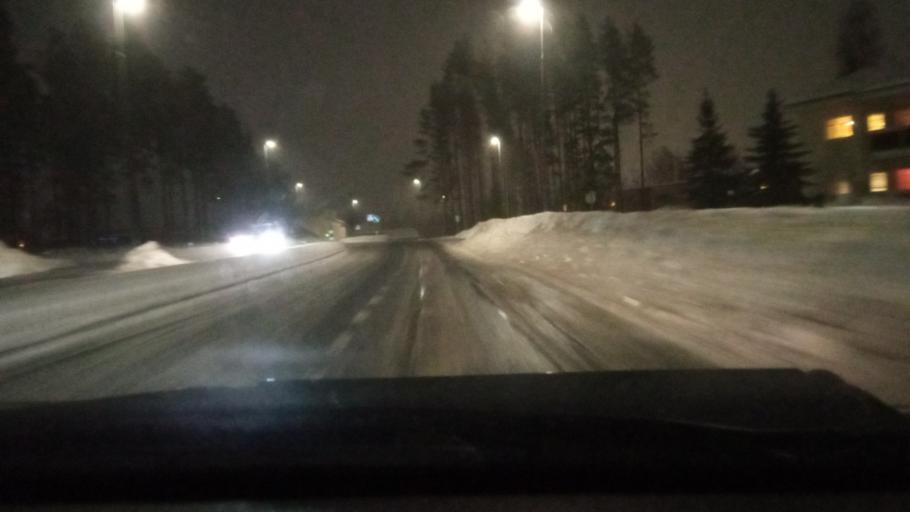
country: FI
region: Southern Ostrobothnia
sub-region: Jaerviseutu
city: Alajaervi
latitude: 63.0031
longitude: 23.8077
